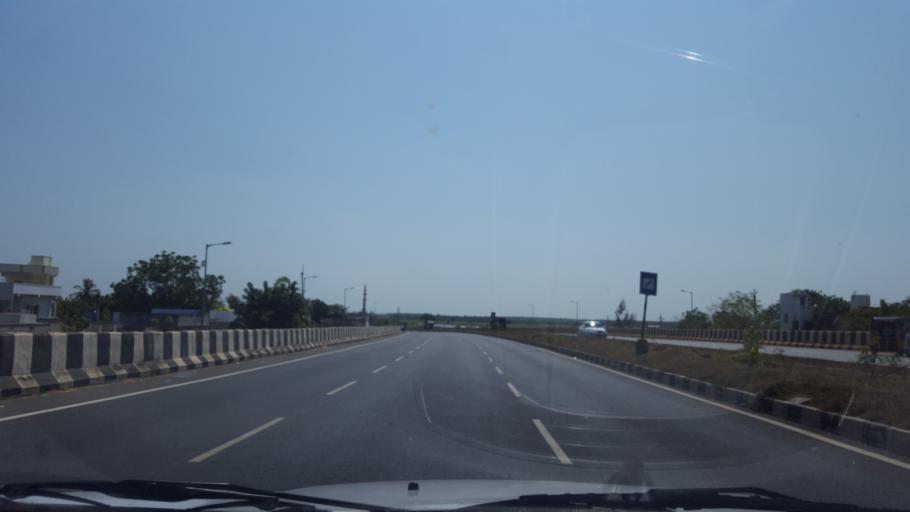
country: IN
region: Andhra Pradesh
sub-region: Nellore
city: Kavali
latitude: 14.8285
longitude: 79.9927
